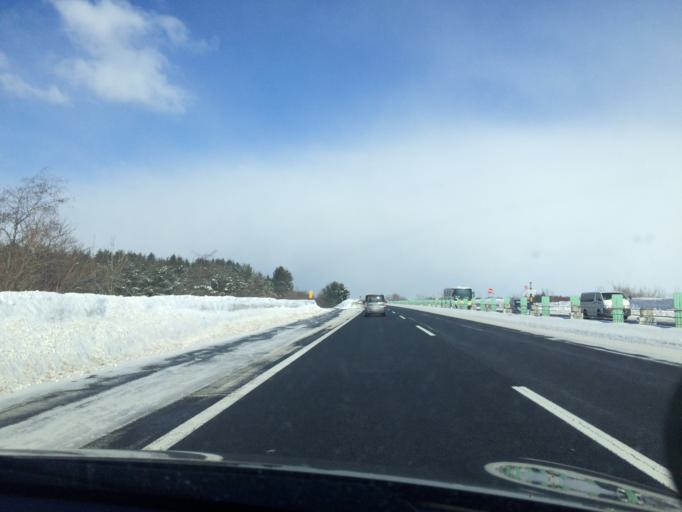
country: JP
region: Hokkaido
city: Kitahiroshima
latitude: 42.9010
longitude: 141.5504
